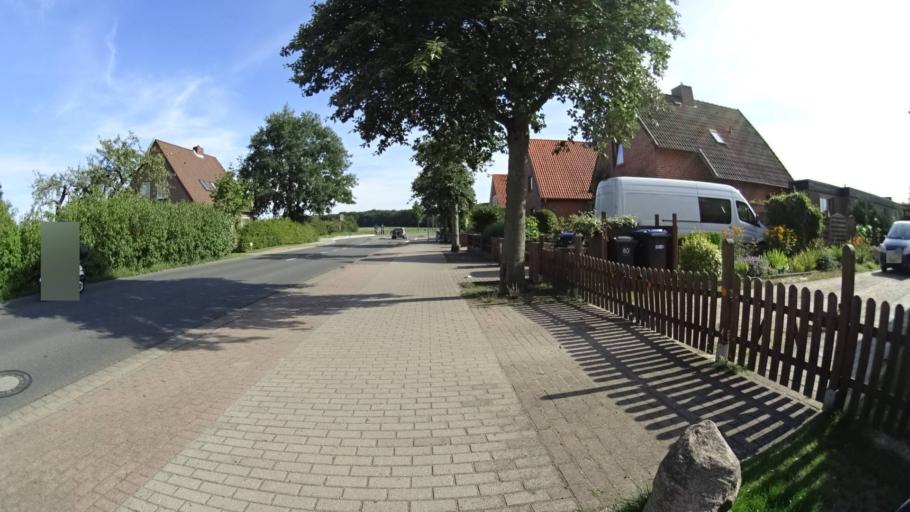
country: DE
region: Lower Saxony
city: Bardowick
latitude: 53.2893
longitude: 10.3961
